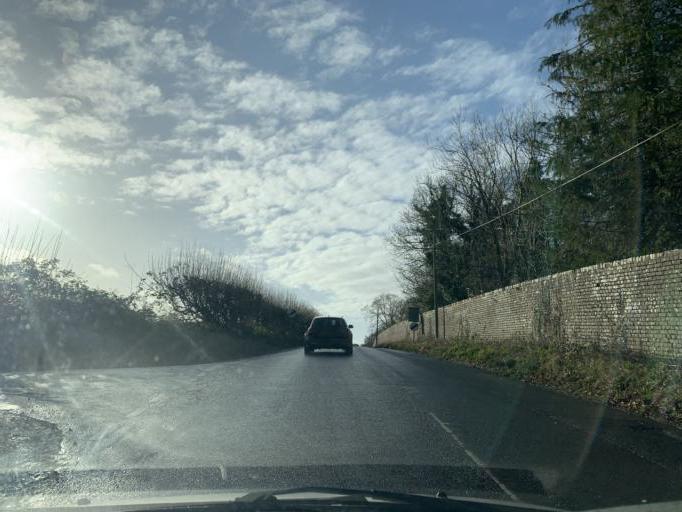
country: GB
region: England
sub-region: Wiltshire
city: Wilton
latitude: 51.0689
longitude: -1.8532
